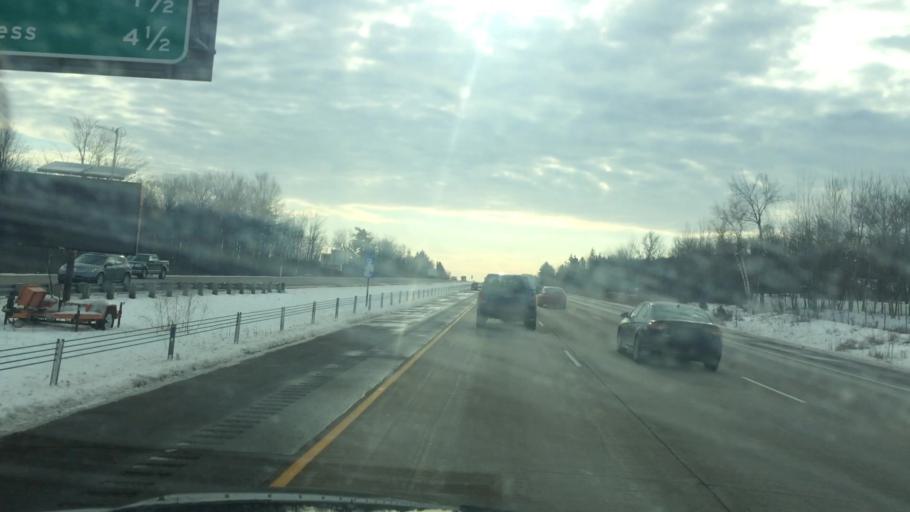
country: US
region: Wisconsin
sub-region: Marathon County
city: Rib Mountain
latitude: 44.9234
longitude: -89.6596
